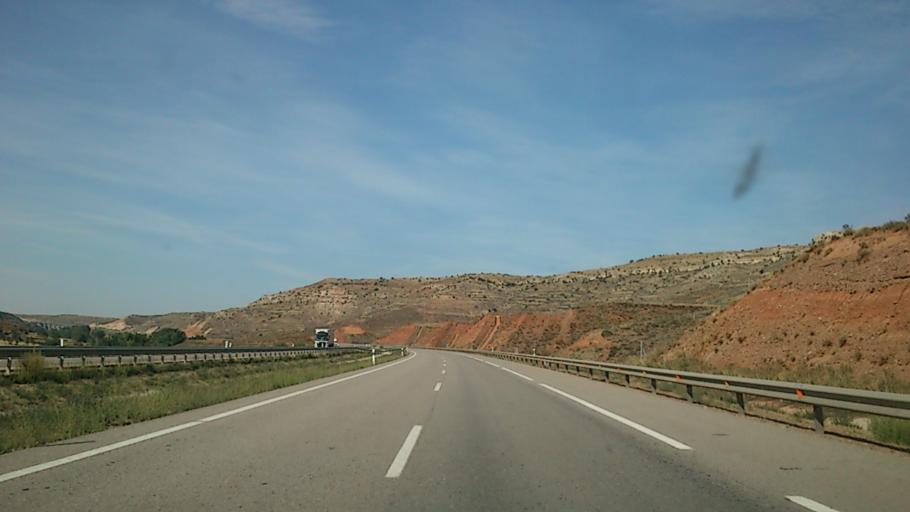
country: ES
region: Aragon
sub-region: Provincia de Teruel
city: Calamocha
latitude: 40.9613
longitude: -1.2639
